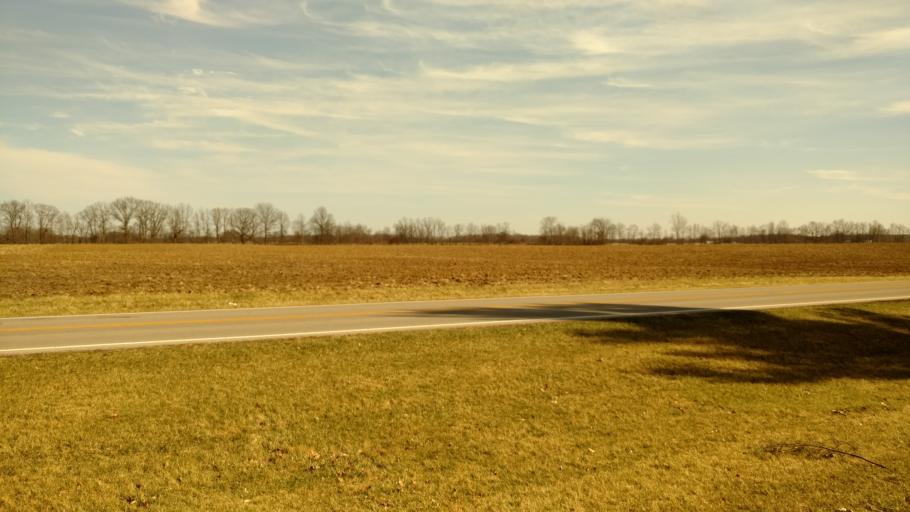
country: US
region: Ohio
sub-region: Hardin County
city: Forest
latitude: 40.6911
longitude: -83.3955
